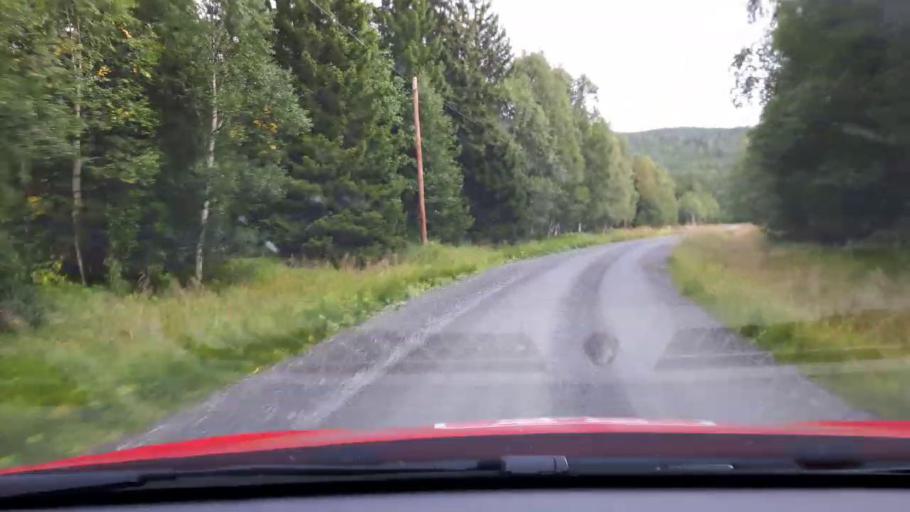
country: SE
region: Jaemtland
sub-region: Are Kommun
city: Are
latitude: 63.7726
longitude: 13.0796
